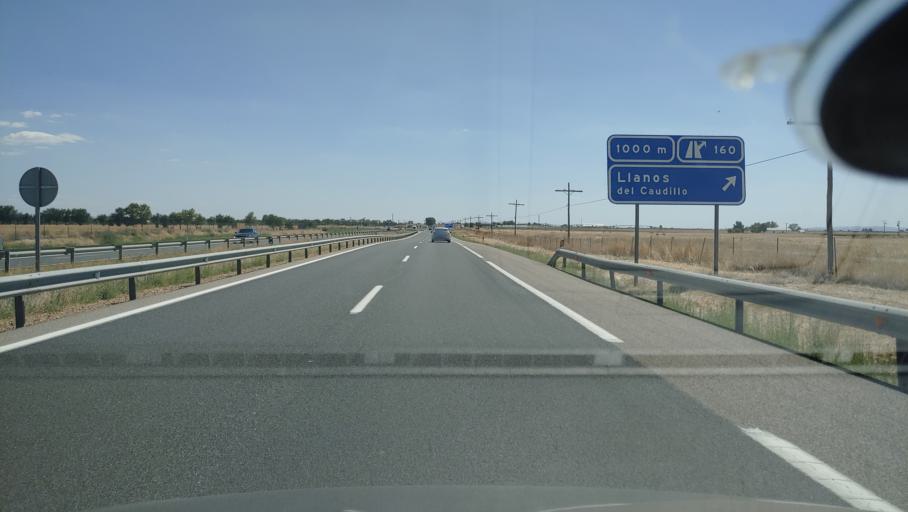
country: ES
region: Castille-La Mancha
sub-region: Provincia de Ciudad Real
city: Villarta de San Juan
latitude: 39.1342
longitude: -3.3808
